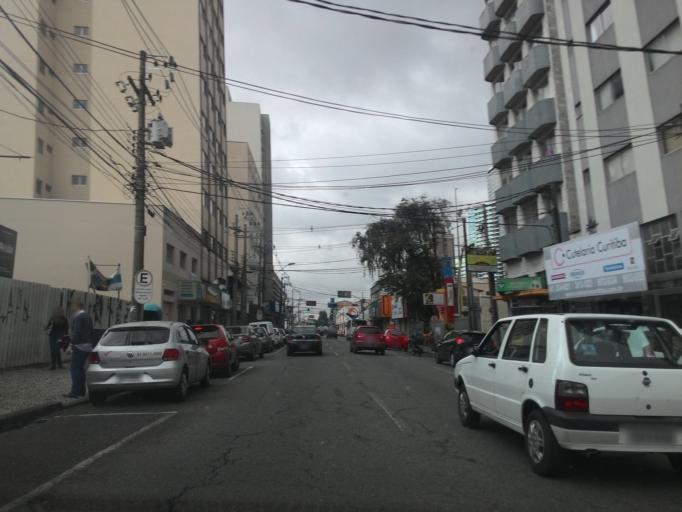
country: BR
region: Parana
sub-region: Curitiba
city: Curitiba
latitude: -25.4329
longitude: -49.2624
